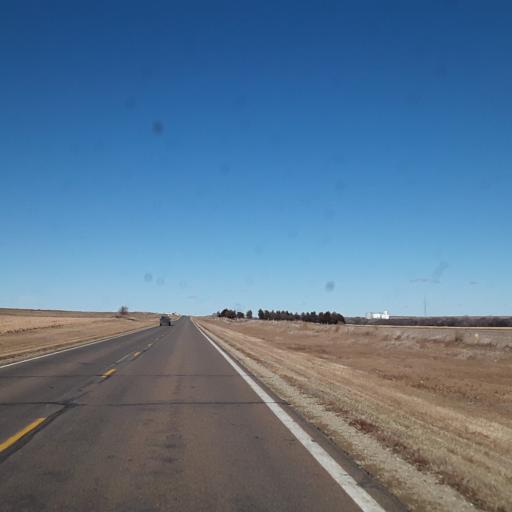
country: US
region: Kansas
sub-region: Lincoln County
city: Lincoln
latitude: 39.0110
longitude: -98.1516
